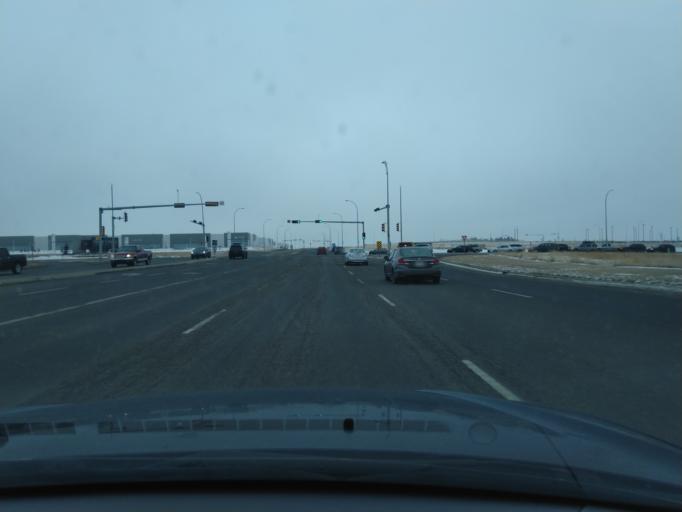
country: CA
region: Alberta
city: Airdrie
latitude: 51.1989
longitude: -113.9910
